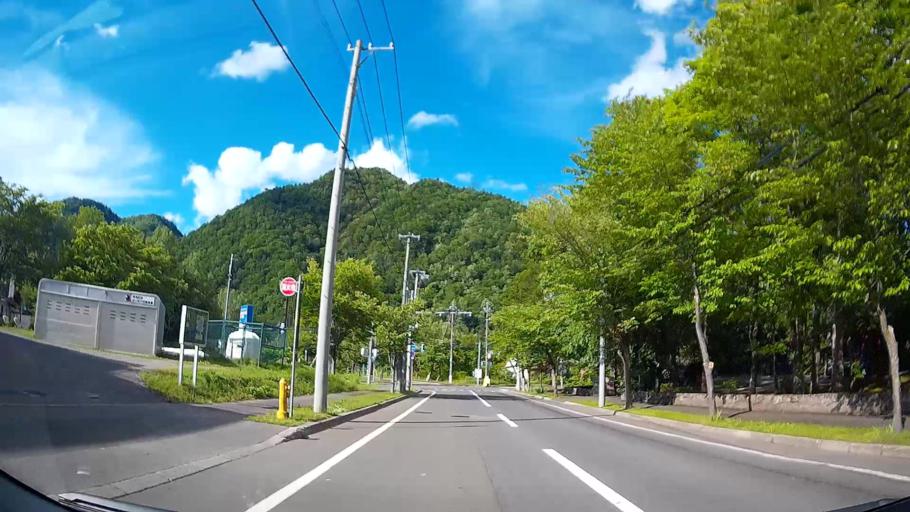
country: JP
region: Hokkaido
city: Sapporo
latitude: 42.9723
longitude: 141.1654
